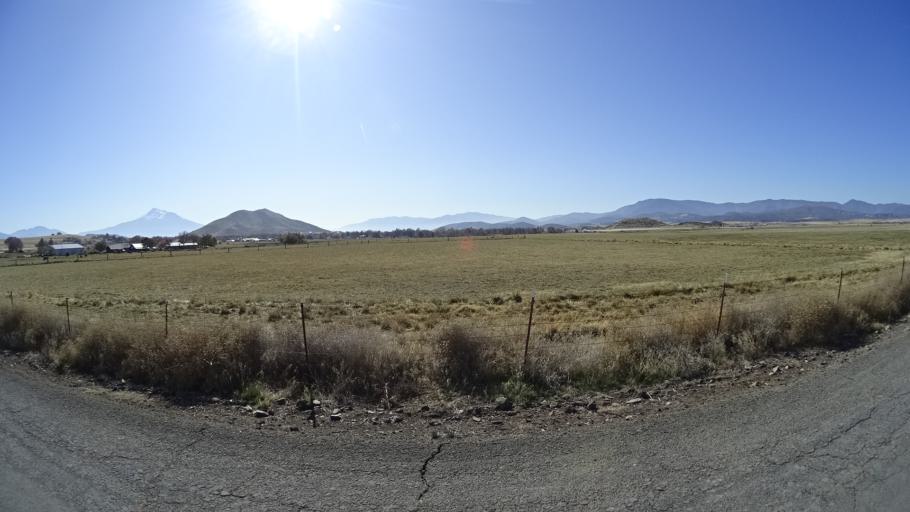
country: US
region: California
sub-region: Siskiyou County
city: Montague
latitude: 41.7420
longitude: -122.5305
